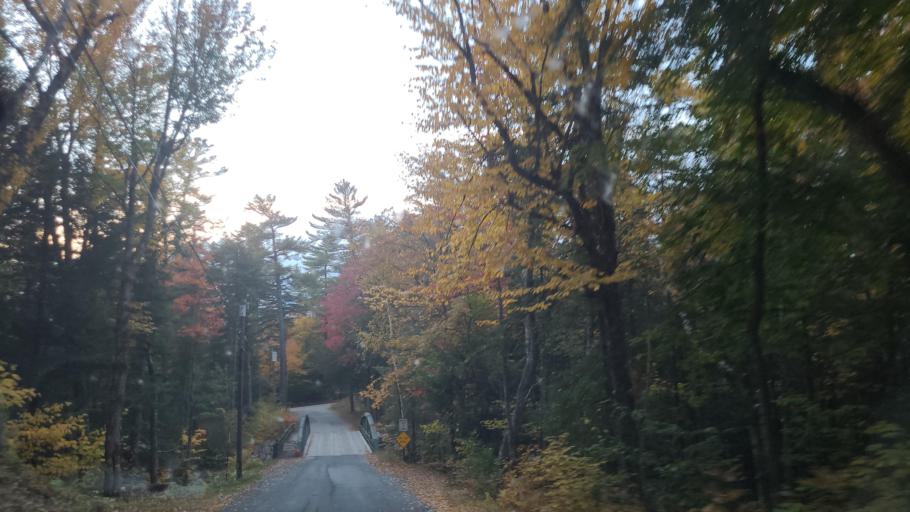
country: US
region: New Hampshire
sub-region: Carroll County
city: North Conway
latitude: 44.1524
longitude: -71.1786
